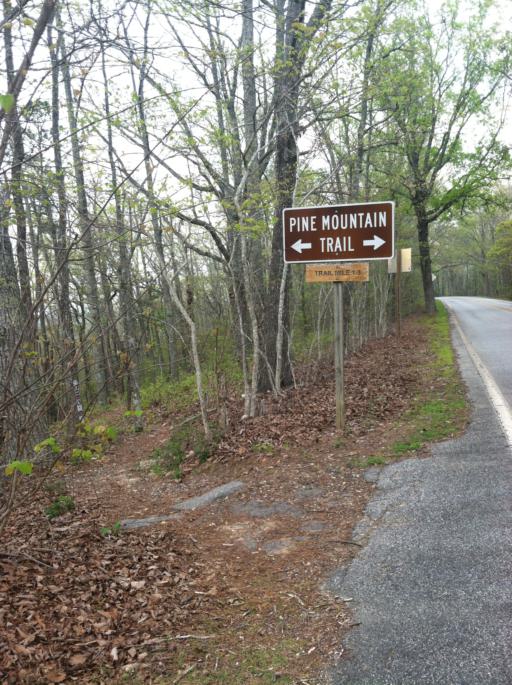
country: US
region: Georgia
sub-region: Harris County
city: Pine Mountain
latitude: 32.8239
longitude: -84.8380
